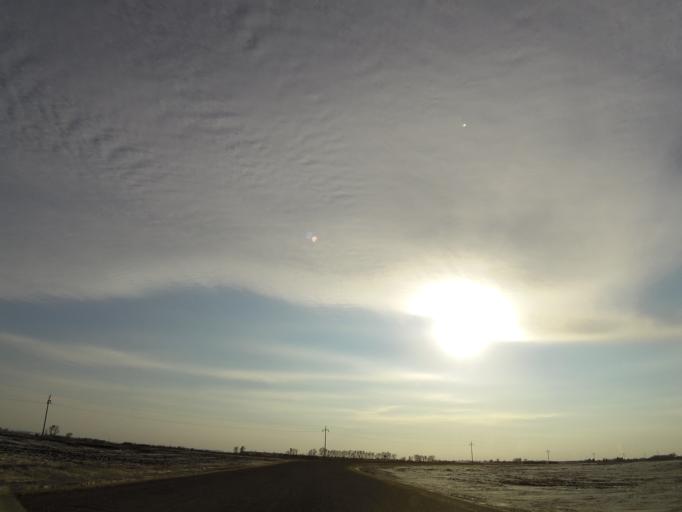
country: US
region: North Dakota
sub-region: Walsh County
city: Grafton
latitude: 48.4209
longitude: -97.3628
